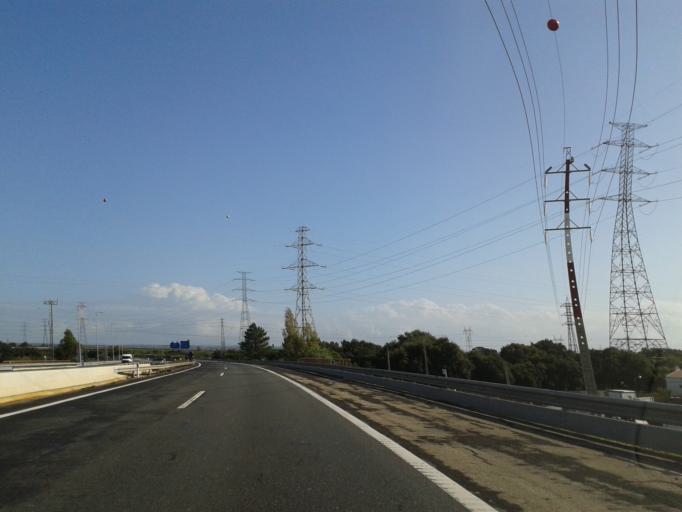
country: PT
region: Setubal
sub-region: Palmela
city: Palmela
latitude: 38.5811
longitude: -8.8703
